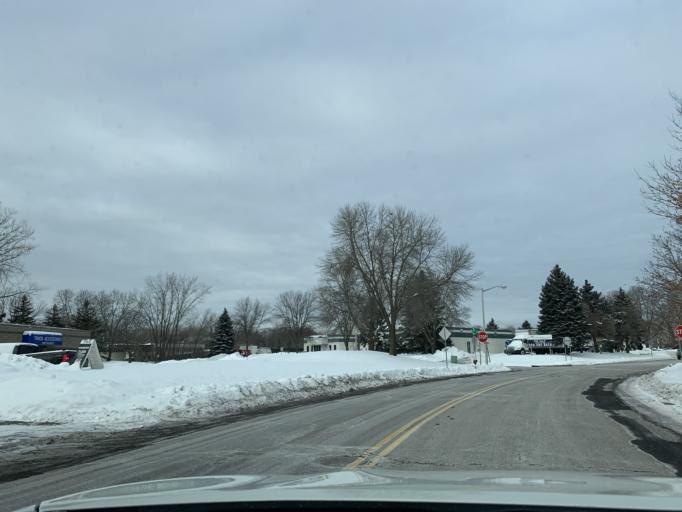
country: US
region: Minnesota
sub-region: Hennepin County
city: West Coon Rapids
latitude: 45.1772
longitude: -93.2976
